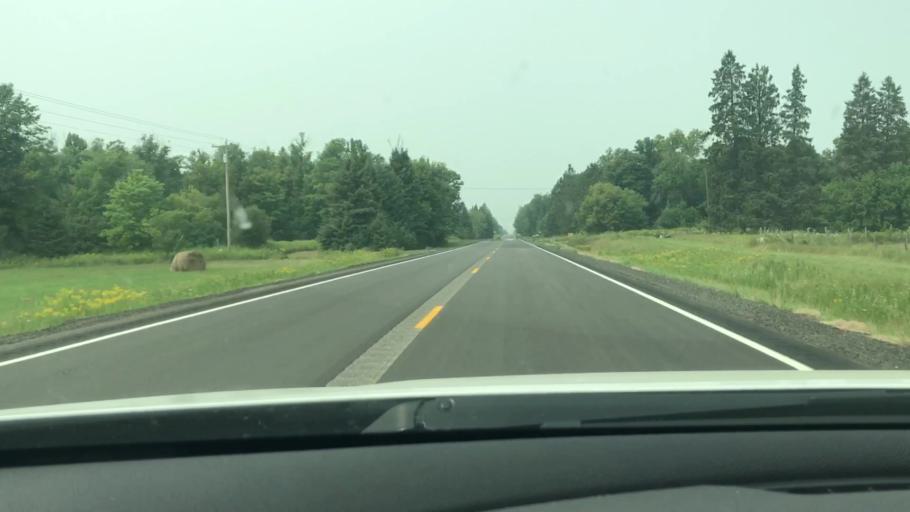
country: US
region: Minnesota
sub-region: Itasca County
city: Cohasset
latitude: 47.3563
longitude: -93.8524
